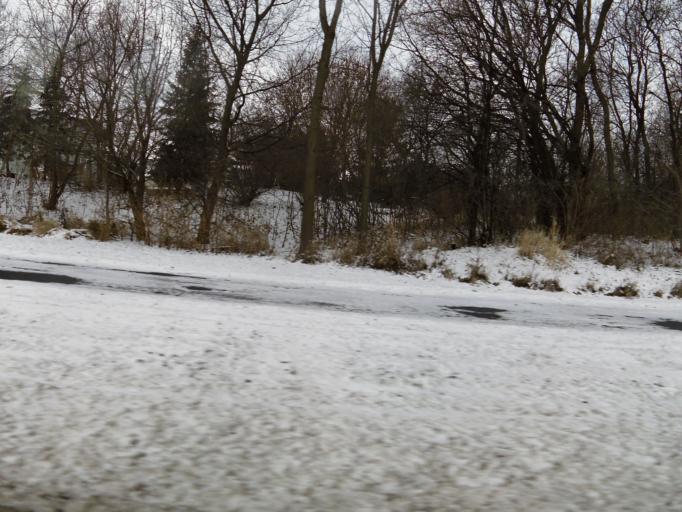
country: US
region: Minnesota
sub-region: Scott County
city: Prior Lake
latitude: 44.7093
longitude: -93.4150
